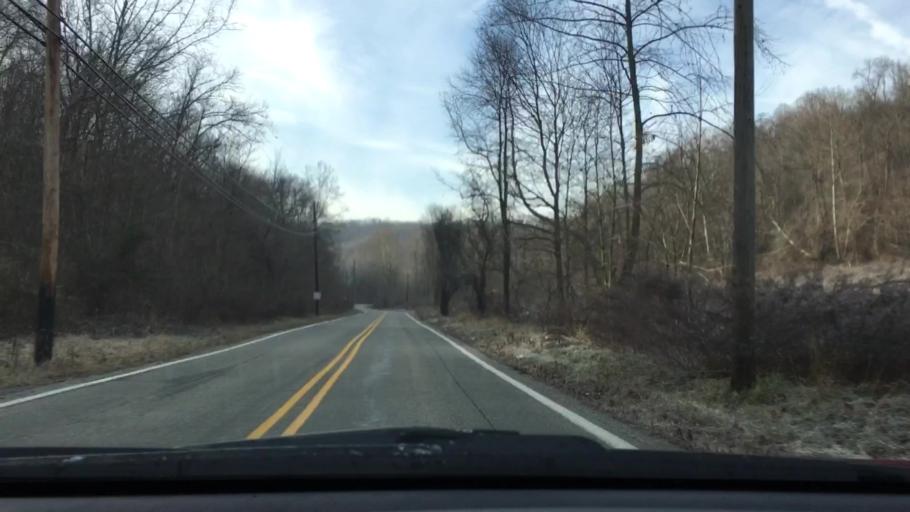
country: US
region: Pennsylvania
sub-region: Allegheny County
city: Industry
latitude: 40.2412
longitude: -79.8146
